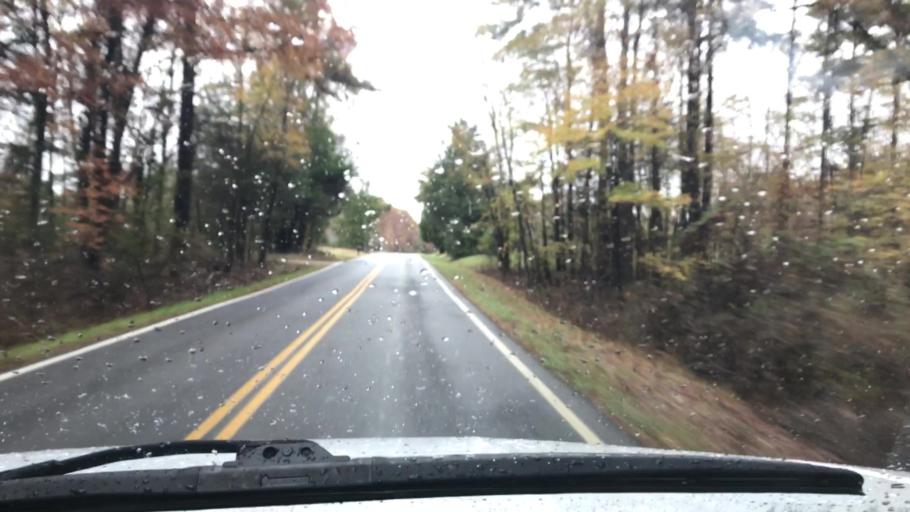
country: US
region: Virginia
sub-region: Henrico County
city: Short Pump
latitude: 37.6187
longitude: -77.6949
